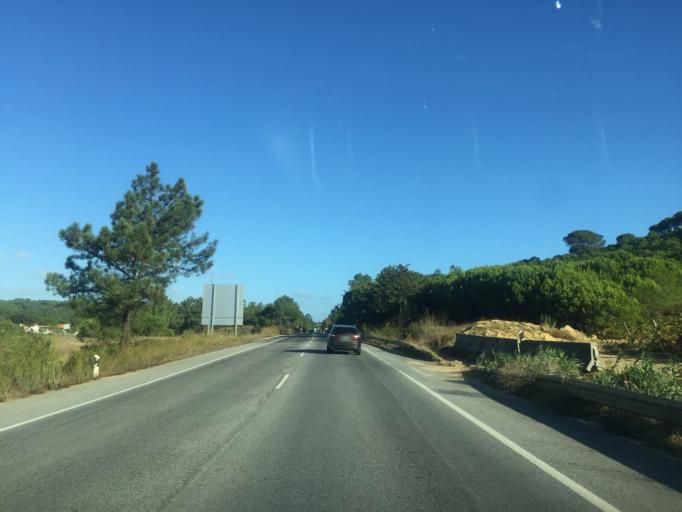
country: PT
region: Lisbon
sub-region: Azambuja
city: Alcoentre
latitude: 39.2169
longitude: -8.9533
